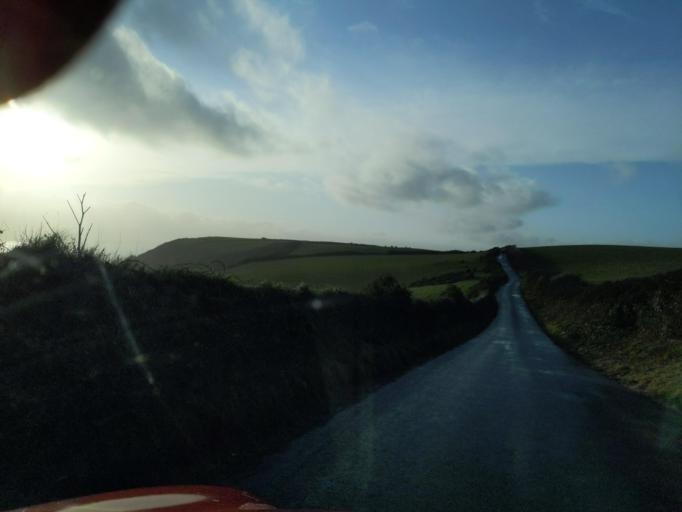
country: GB
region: England
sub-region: Cornwall
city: Fowey
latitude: 50.3314
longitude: -4.6075
